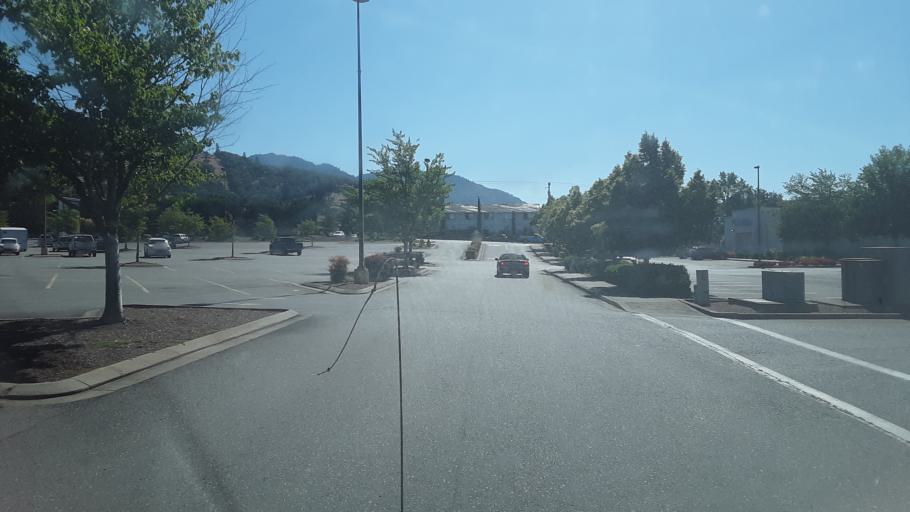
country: US
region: Oregon
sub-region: Josephine County
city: Fruitdale
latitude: 42.4379
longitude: -123.3095
